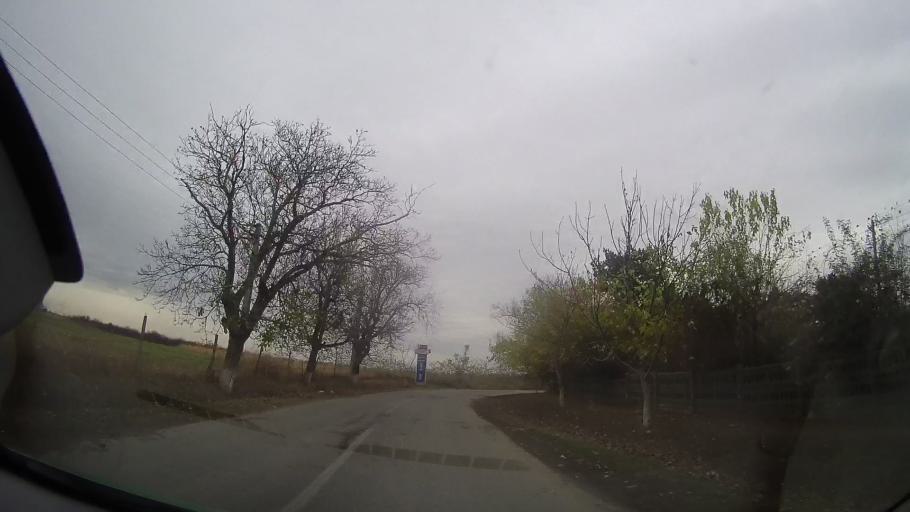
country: RO
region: Prahova
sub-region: Comuna Vadu Sapat
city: Vadu Sapat
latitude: 45.0270
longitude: 26.3918
